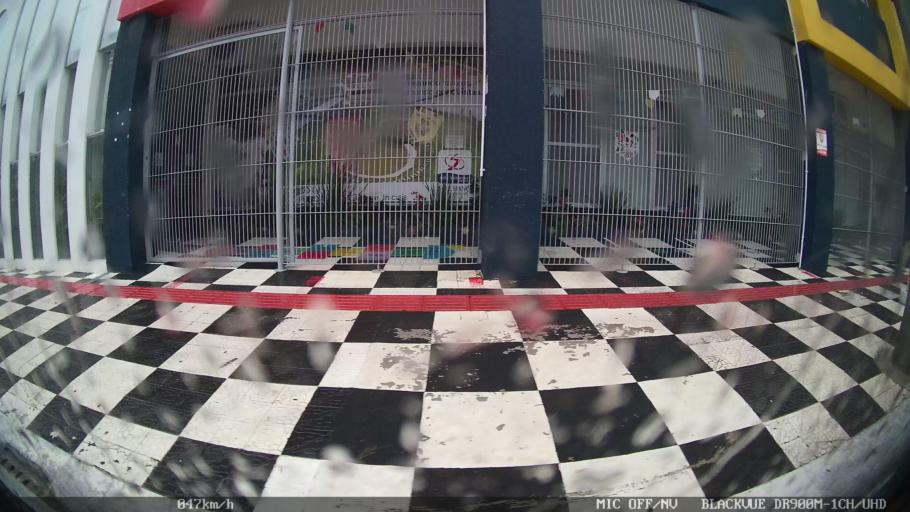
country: BR
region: Santa Catarina
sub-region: Balneario Camboriu
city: Balneario Camboriu
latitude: -26.9915
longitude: -48.6421
